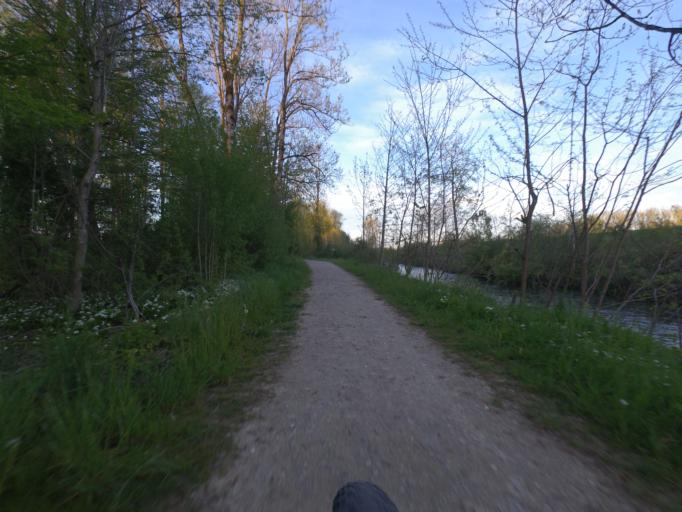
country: CH
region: Thurgau
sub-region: Frauenfeld District
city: Pfyn
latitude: 47.5912
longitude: 8.9601
